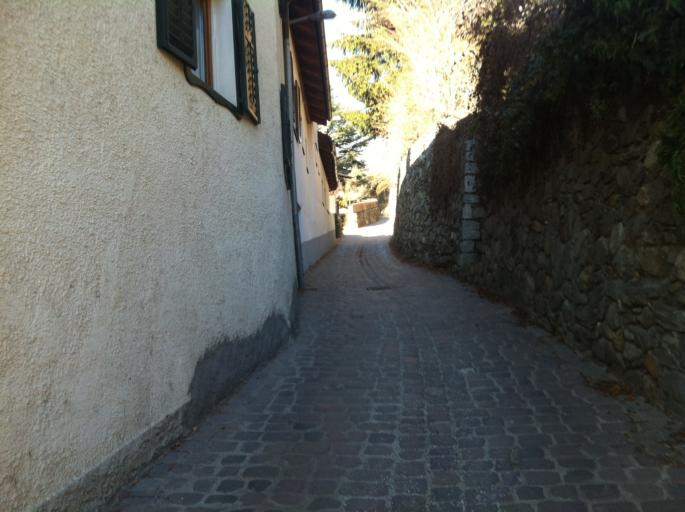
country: IT
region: Trentino-Alto Adige
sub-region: Bolzano
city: Bressanone
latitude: 46.7190
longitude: 11.6607
